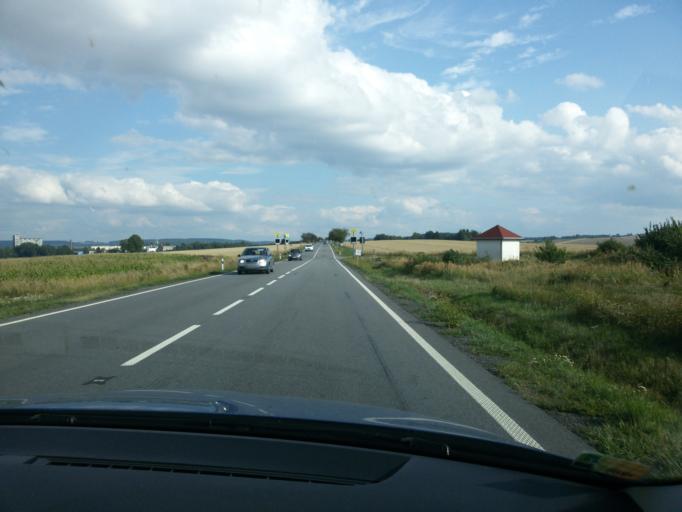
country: CZ
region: Pardubicky
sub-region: Okres Svitavy
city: Policka
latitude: 49.7224
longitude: 16.2356
